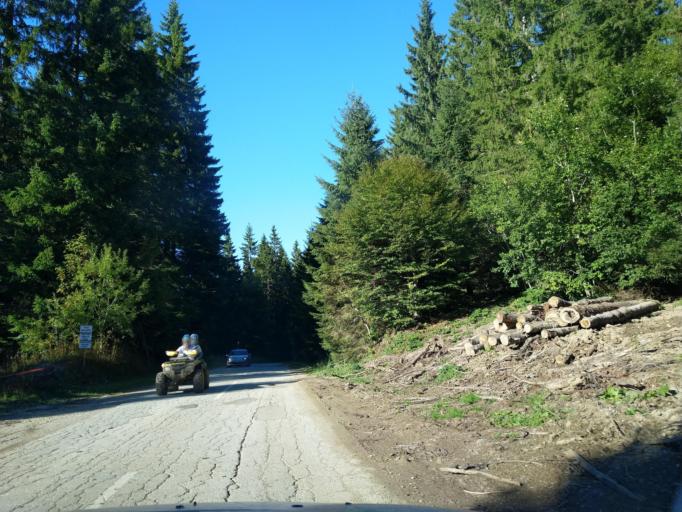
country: RS
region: Central Serbia
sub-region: Moravicki Okrug
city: Ivanjica
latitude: 43.4242
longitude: 20.2637
